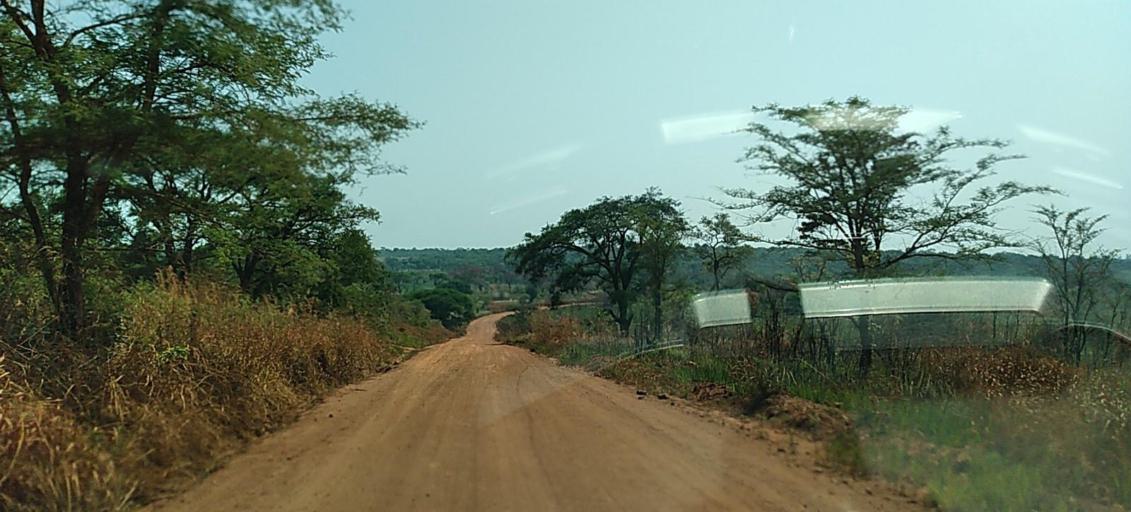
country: ZM
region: North-Western
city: Kansanshi
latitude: -12.0061
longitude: 26.5546
